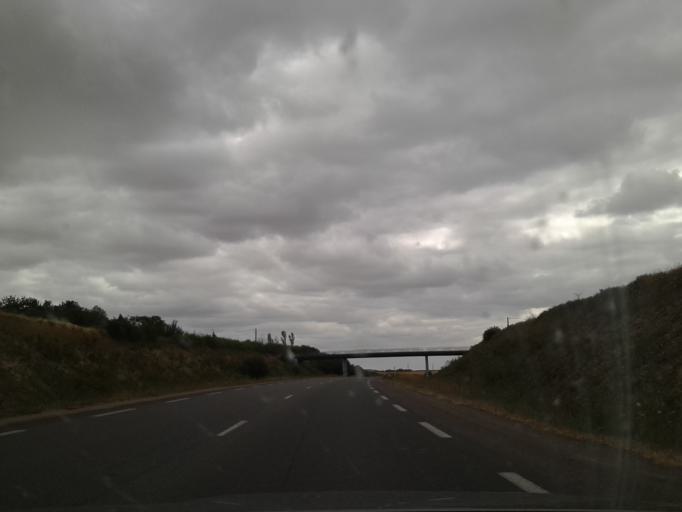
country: FR
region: Centre
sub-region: Departement du Cher
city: La Chapelle-Saint-Ursin
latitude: 47.0666
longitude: 2.3509
